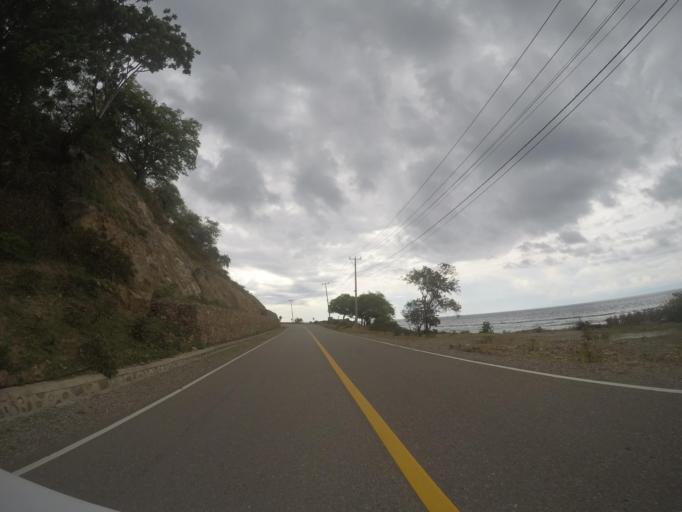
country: TL
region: Bobonaro
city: Maliana
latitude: -8.8178
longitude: 125.0768
